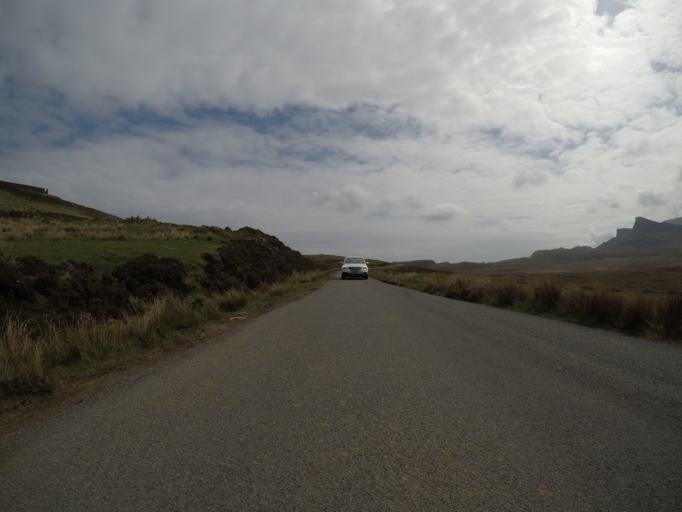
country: GB
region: Scotland
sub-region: Highland
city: Portree
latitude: 57.6807
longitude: -6.2787
